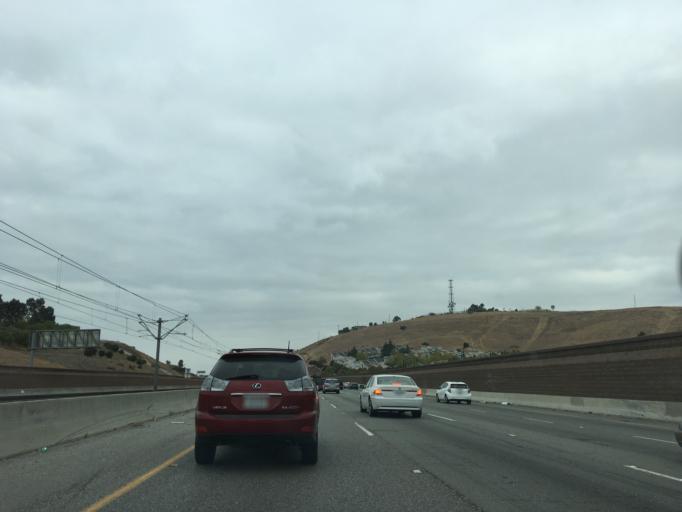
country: US
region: California
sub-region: Santa Clara County
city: Seven Trees
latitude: 37.2806
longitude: -121.8652
